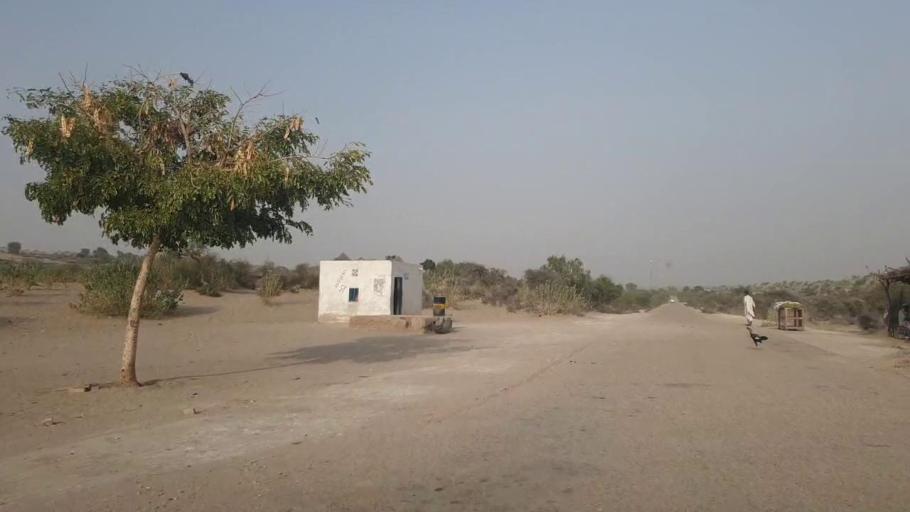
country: PK
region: Sindh
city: Chor
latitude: 25.4169
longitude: 69.9736
